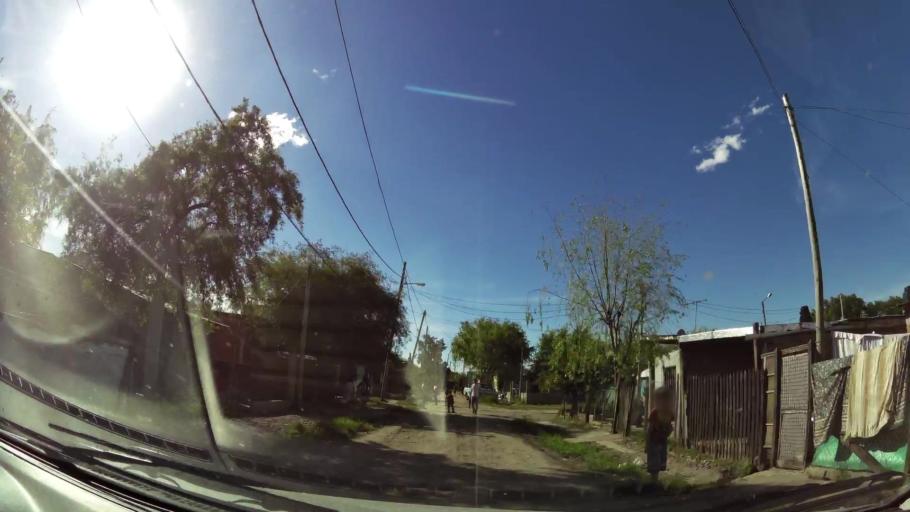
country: AR
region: Buenos Aires
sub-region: Partido de Almirante Brown
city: Adrogue
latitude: -34.8266
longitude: -58.3422
